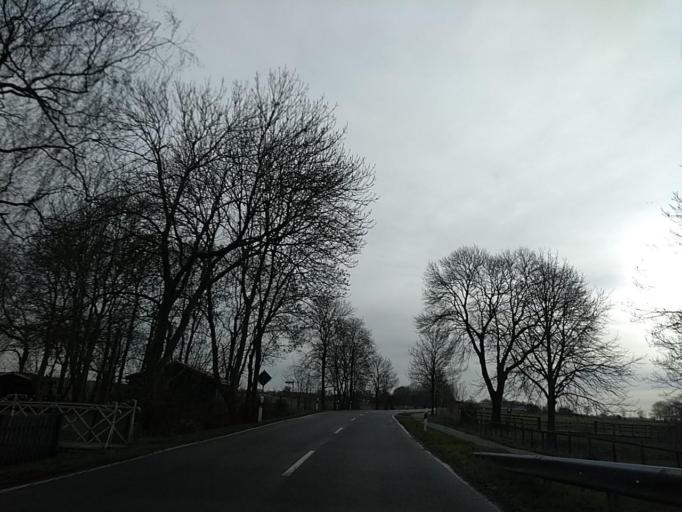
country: DE
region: Lower Saxony
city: Jemgum
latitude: 53.2959
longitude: 7.3514
